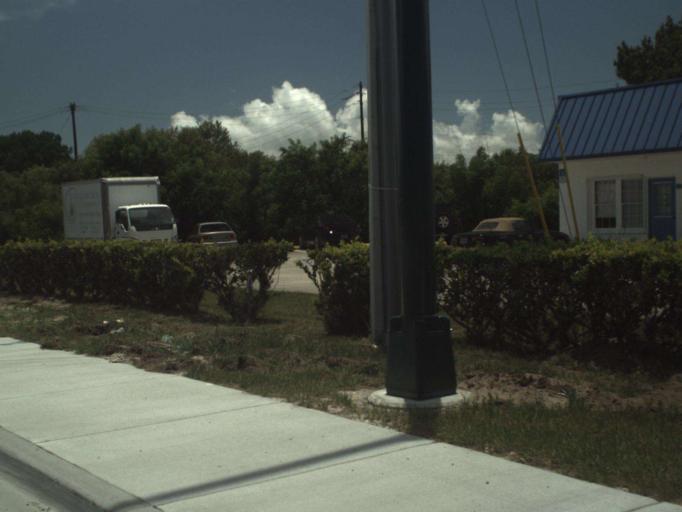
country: US
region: Florida
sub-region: Indian River County
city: Florida Ridge
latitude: 27.5795
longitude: -80.3761
